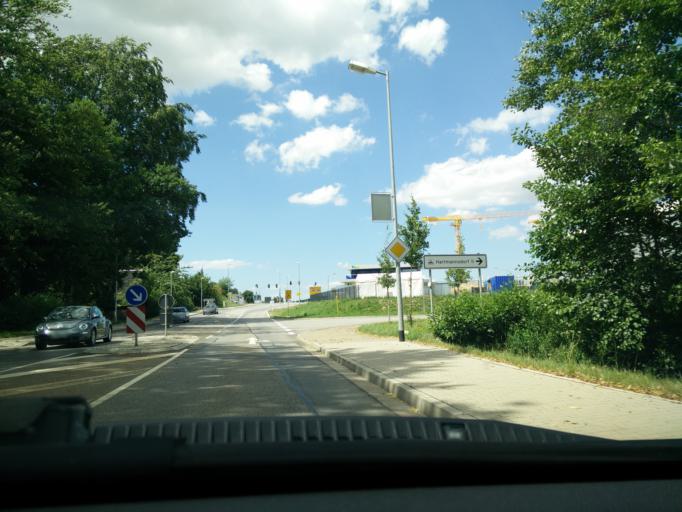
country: DE
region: Saxony
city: Hartmannsdorf
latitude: 50.8910
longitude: 12.7912
